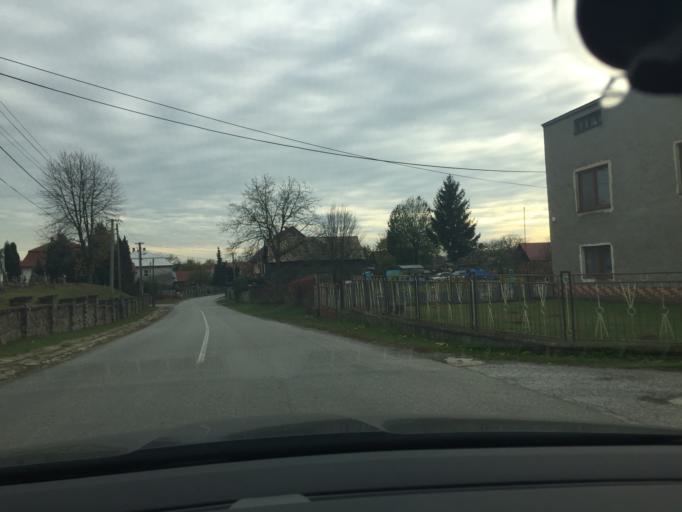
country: SK
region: Kosicky
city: Kosice
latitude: 48.8172
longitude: 21.3251
